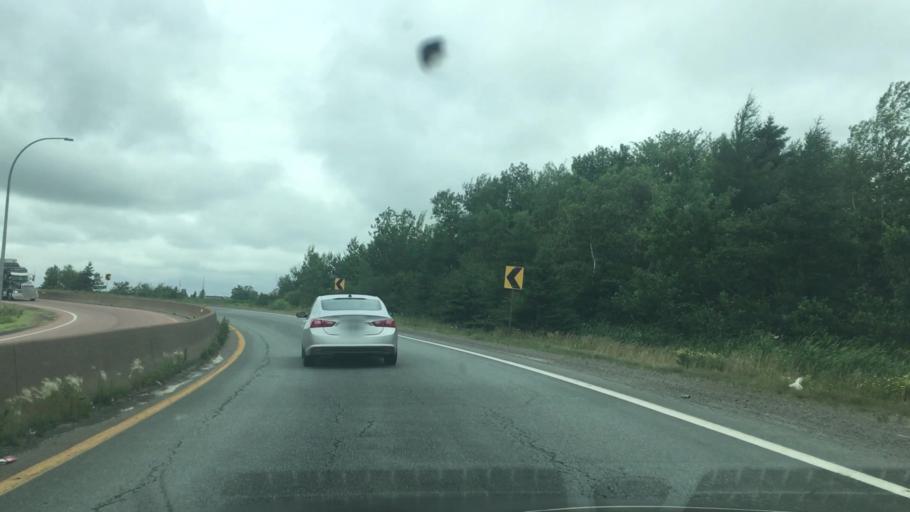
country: CA
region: Nova Scotia
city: Truro
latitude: 45.3915
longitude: -63.3268
